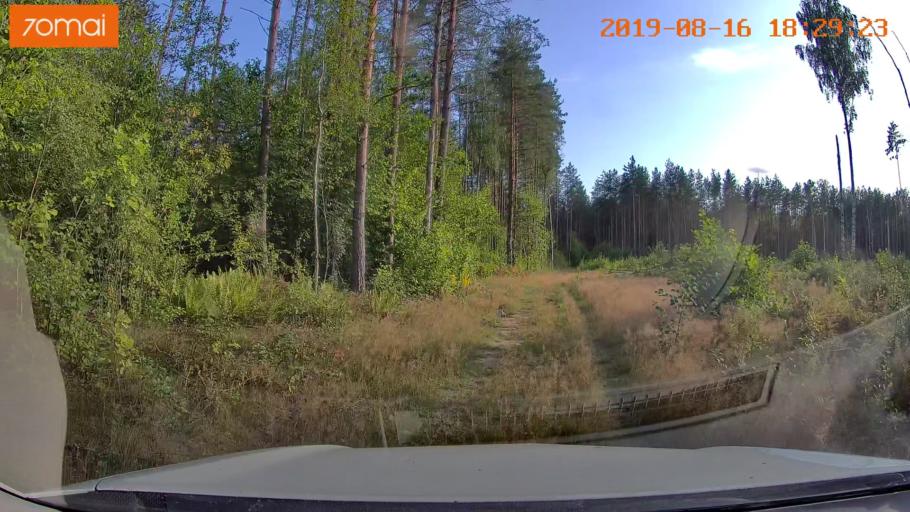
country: BY
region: Mogilev
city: Asipovichy
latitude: 53.1982
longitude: 28.6392
